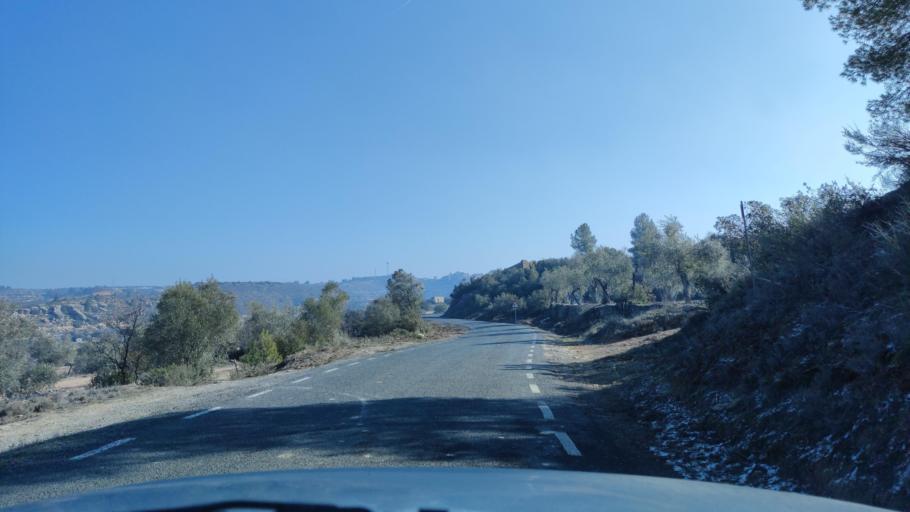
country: ES
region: Catalonia
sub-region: Provincia de Lleida
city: Torrebesses
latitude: 41.4306
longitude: 0.5814
